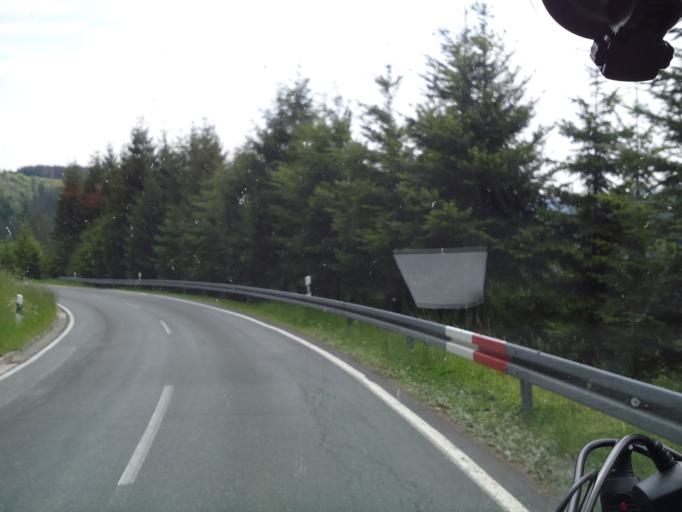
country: DE
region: Bavaria
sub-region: Upper Franconia
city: Steinwiesen
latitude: 50.3029
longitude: 11.4420
